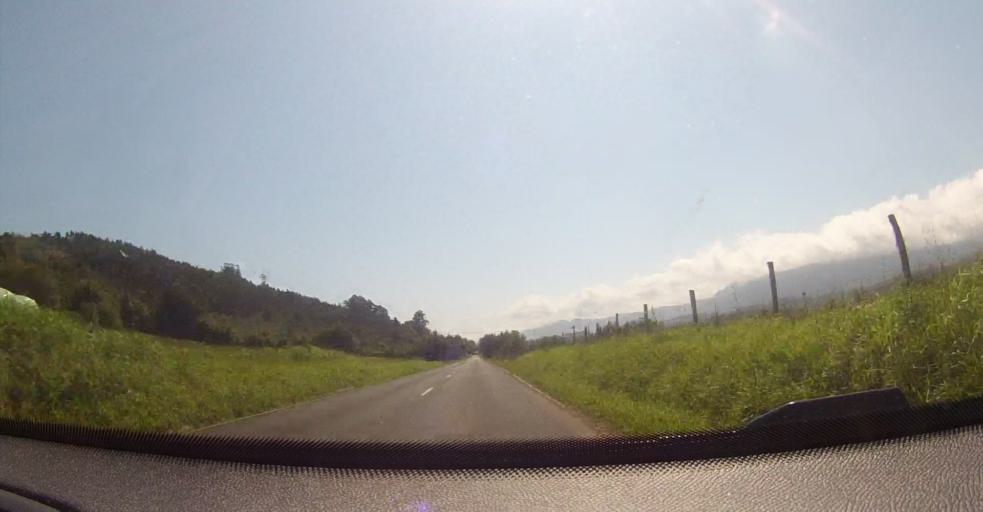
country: ES
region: Asturias
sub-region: Province of Asturias
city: Colunga
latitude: 43.4889
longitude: -5.3041
